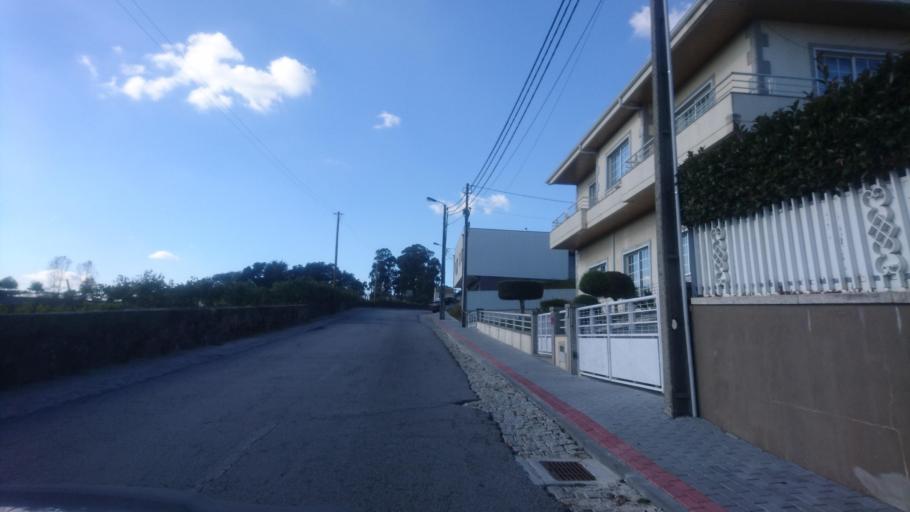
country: PT
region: Porto
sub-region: Paredes
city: Madalena
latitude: 41.2332
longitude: -8.3596
